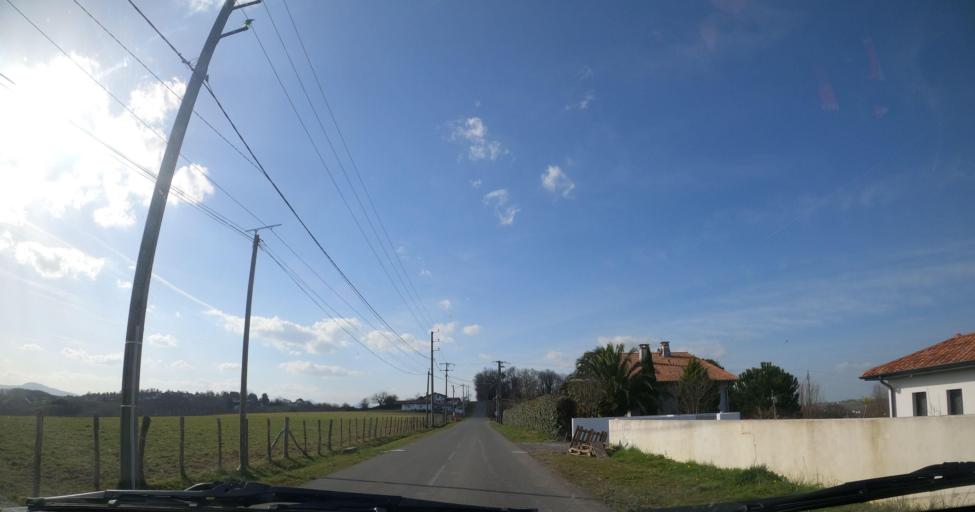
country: FR
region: Aquitaine
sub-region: Departement des Pyrenees-Atlantiques
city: Lahonce
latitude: 43.4384
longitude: -1.3758
